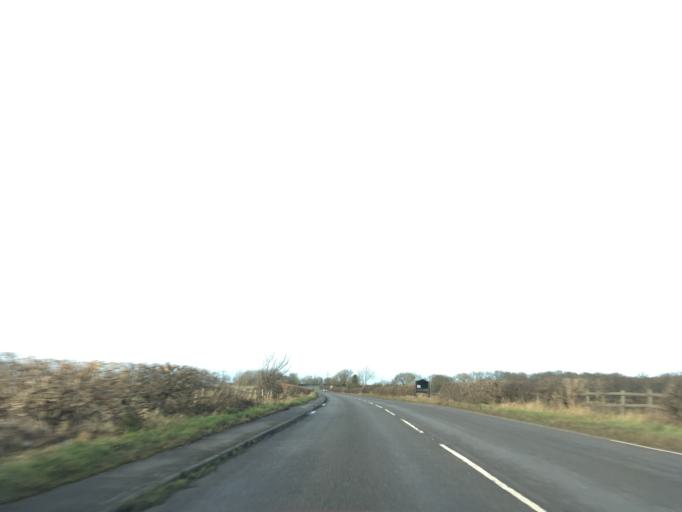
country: GB
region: England
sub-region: Nottinghamshire
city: South Collingham
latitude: 53.1557
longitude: -0.7583
